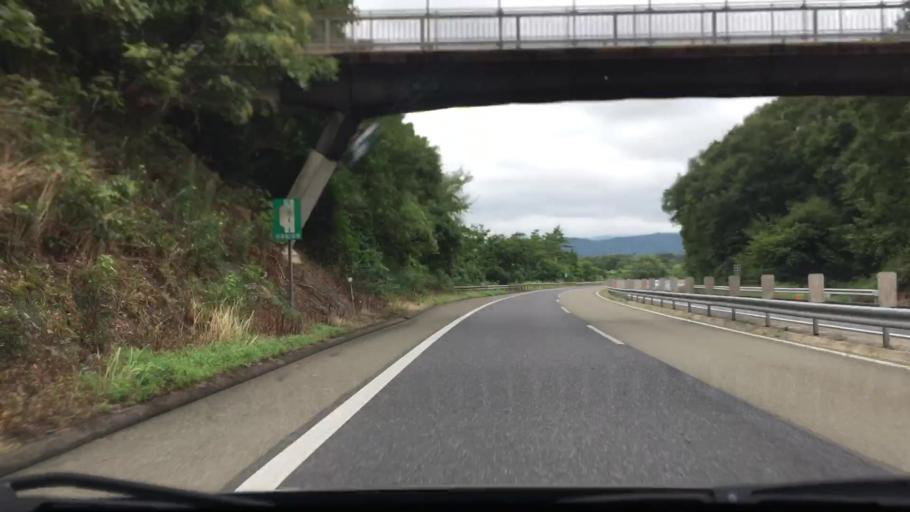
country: JP
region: Hiroshima
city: Shobara
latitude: 34.8308
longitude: 133.0473
